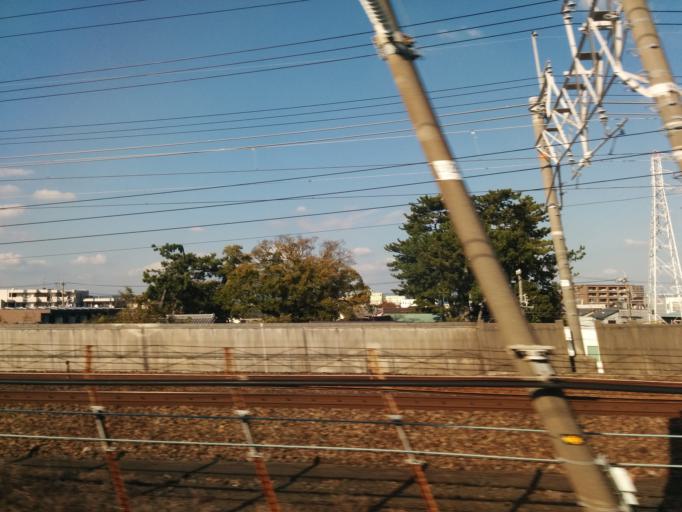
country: JP
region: Shizuoka
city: Hamamatsu
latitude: 34.7086
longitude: 137.7585
